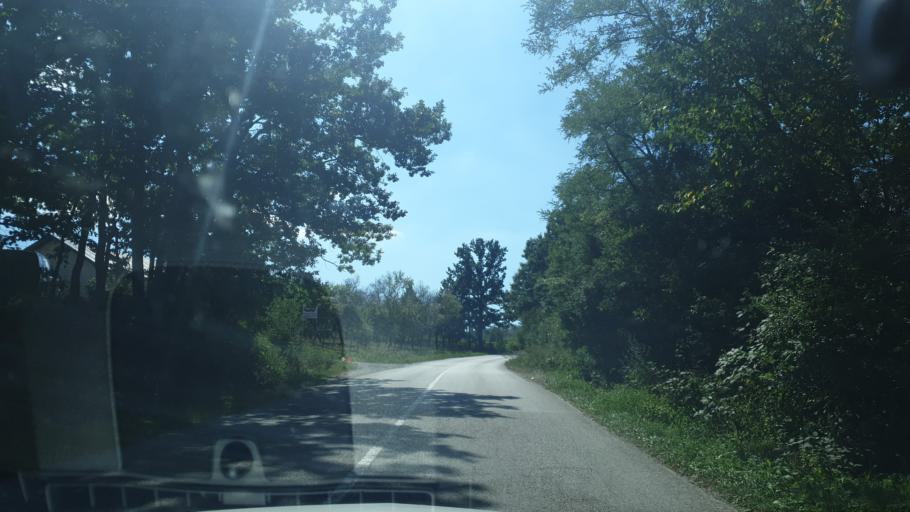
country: RS
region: Central Serbia
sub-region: Zlatiborski Okrug
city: Kosjeric
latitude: 44.0412
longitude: 20.0202
